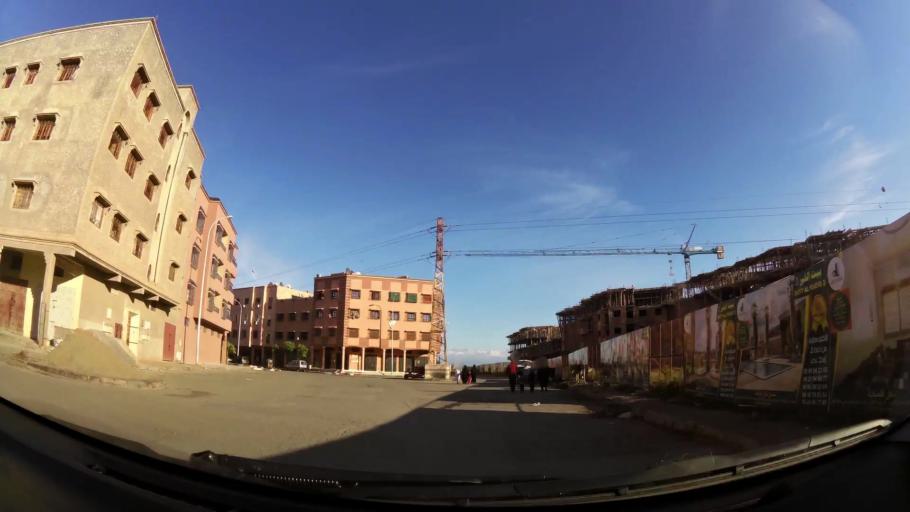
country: MA
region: Marrakech-Tensift-Al Haouz
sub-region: Marrakech
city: Marrakesh
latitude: 31.6155
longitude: -8.0653
